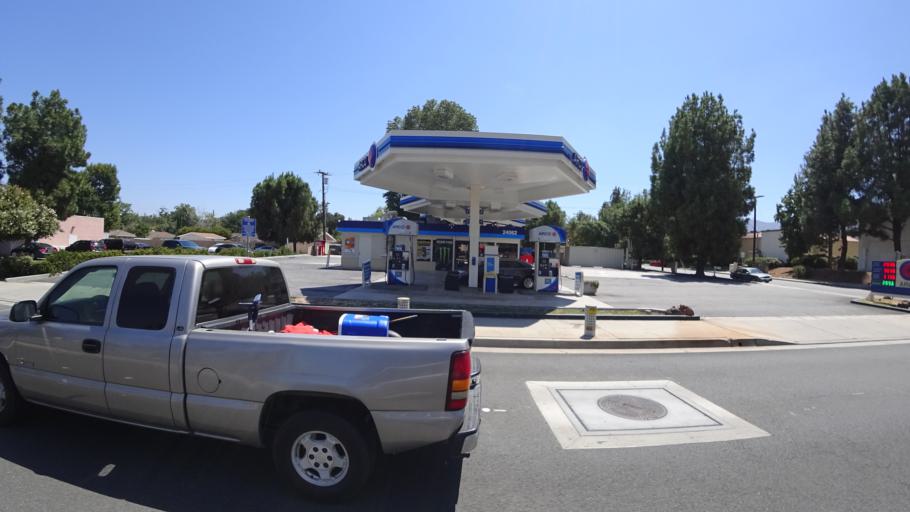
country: US
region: California
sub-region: Los Angeles County
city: Santa Clarita
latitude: 34.3788
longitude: -118.5561
